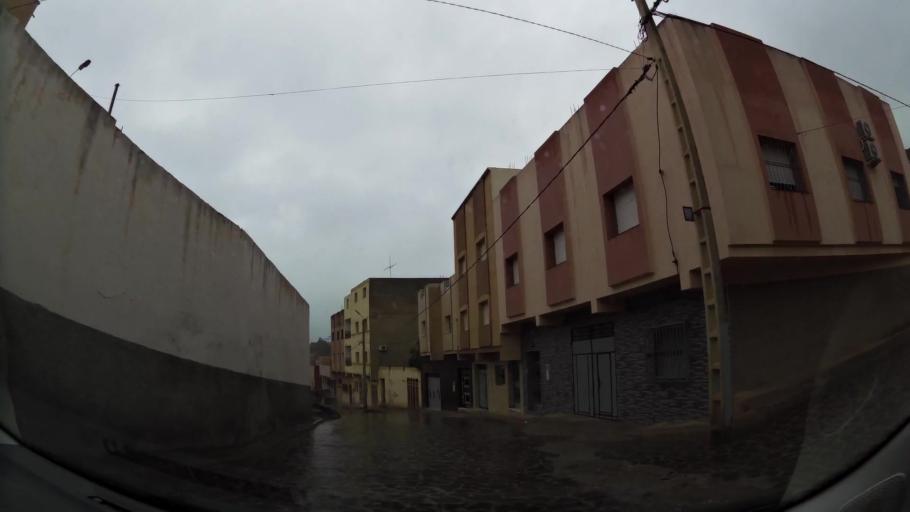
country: MA
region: Oriental
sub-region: Nador
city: Nador
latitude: 35.1809
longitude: -2.9375
